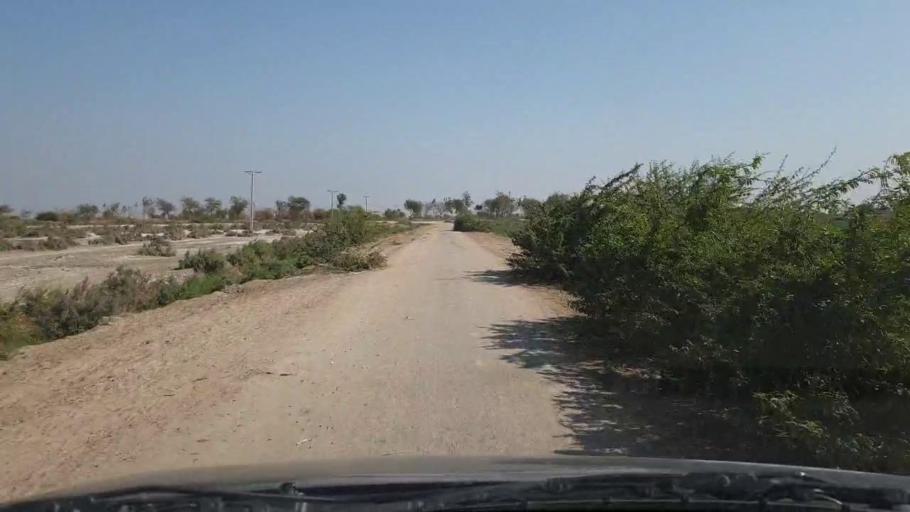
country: PK
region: Sindh
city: Samaro
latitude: 25.1936
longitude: 69.3042
